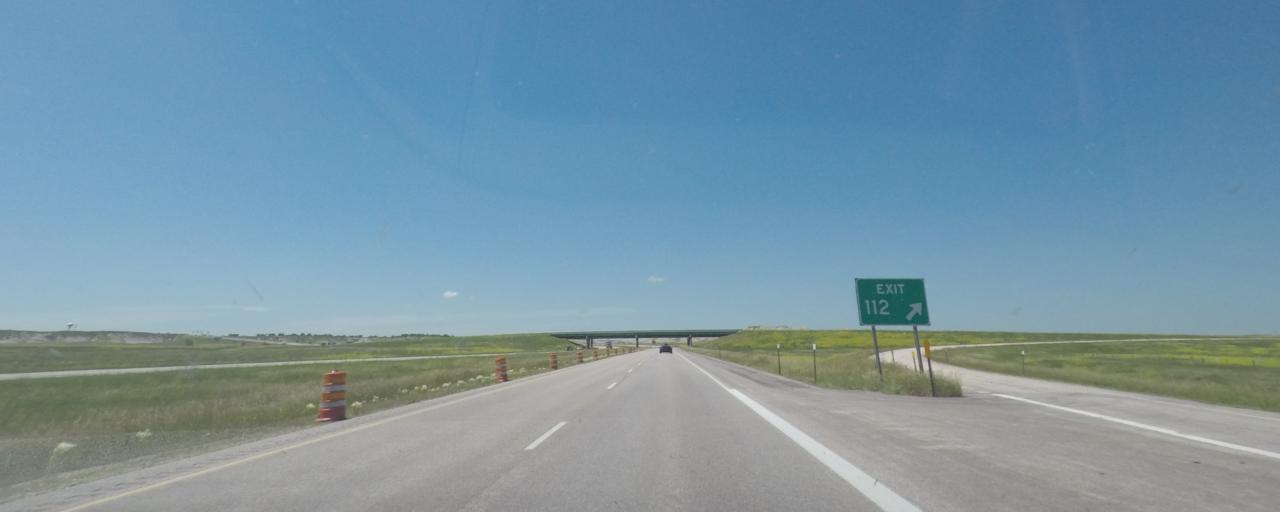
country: US
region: South Dakota
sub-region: Haakon County
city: Philip
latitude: 43.9828
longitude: -102.2038
